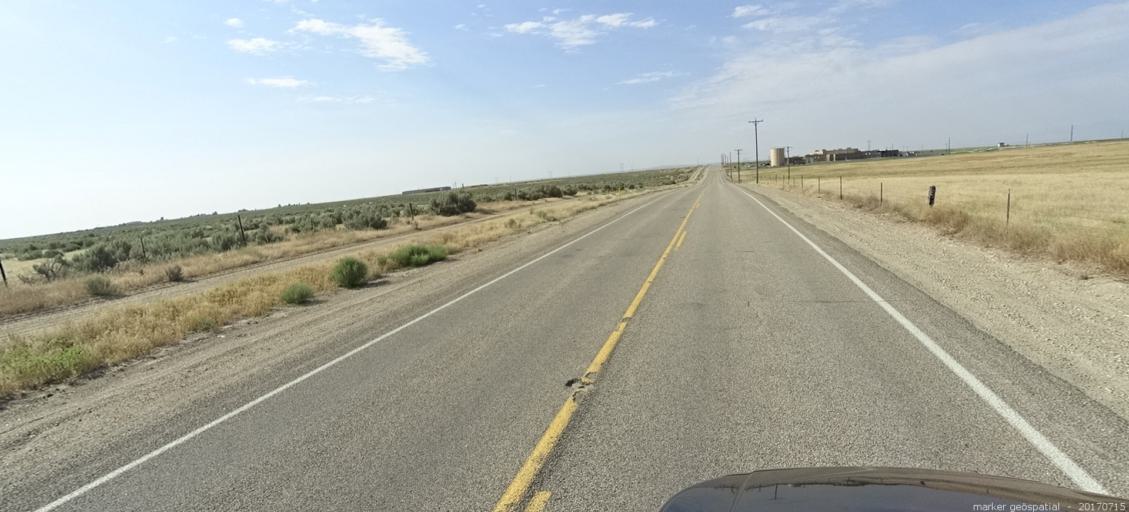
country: US
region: Idaho
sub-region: Ada County
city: Boise
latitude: 43.4663
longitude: -116.2343
